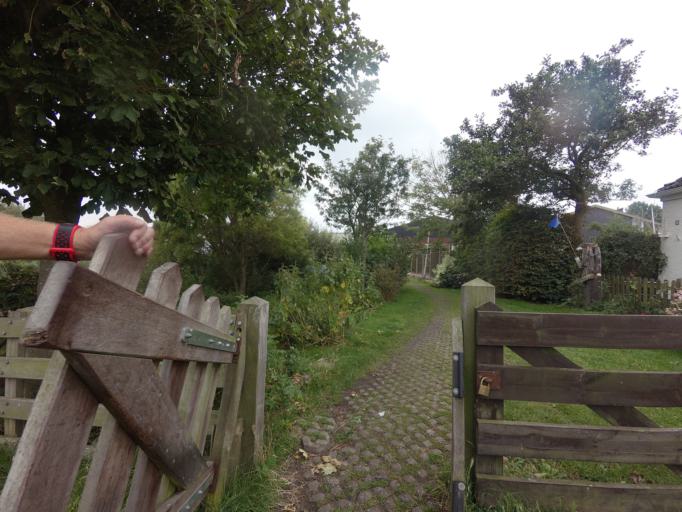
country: NL
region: Friesland
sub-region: Sudwest Fryslan
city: Koudum
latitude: 52.8889
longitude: 5.3582
